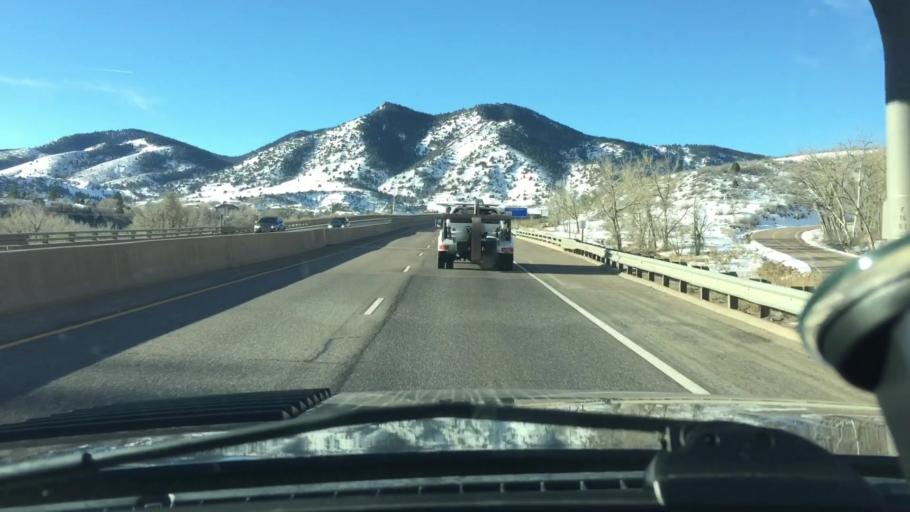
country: US
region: Colorado
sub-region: Jefferson County
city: Indian Hills
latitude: 39.6289
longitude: -105.1785
